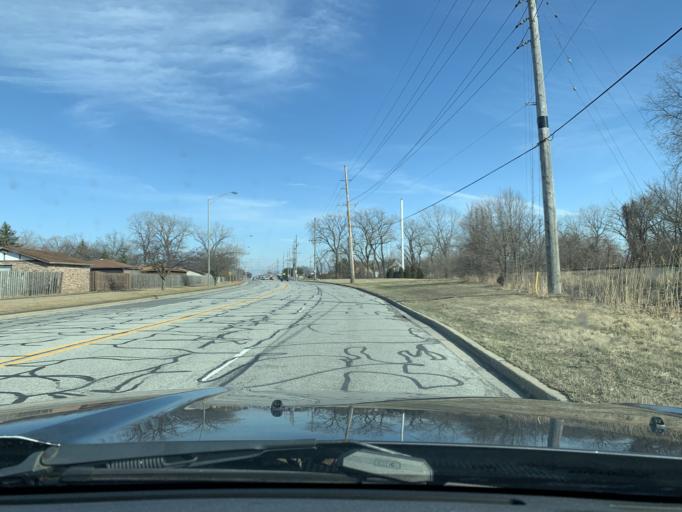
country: US
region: Indiana
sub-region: Lake County
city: Munster
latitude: 41.5378
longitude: -87.4943
